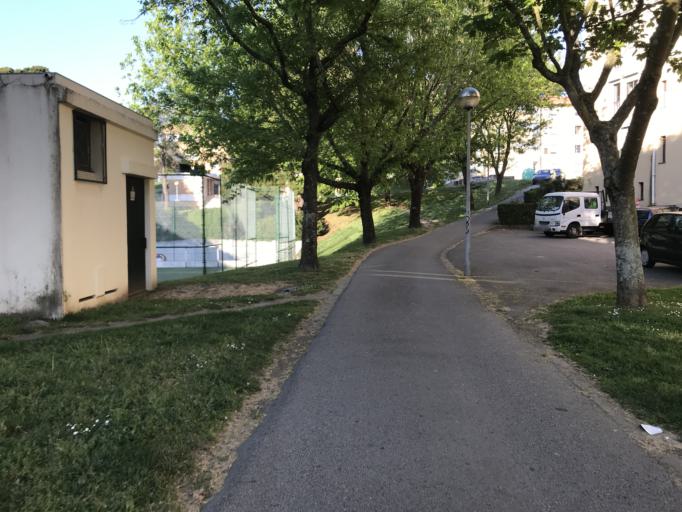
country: PT
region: Porto
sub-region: Matosinhos
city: Matosinhos
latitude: 41.1811
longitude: -8.6745
